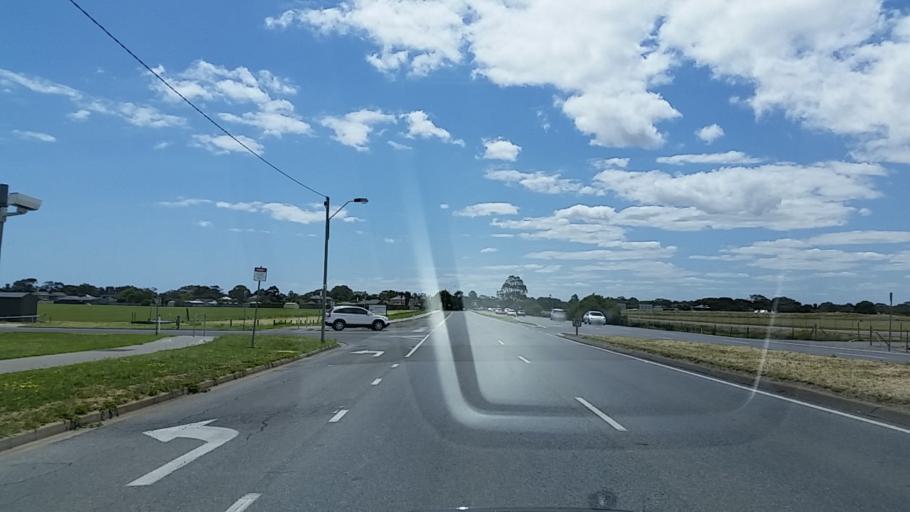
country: AU
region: South Australia
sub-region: Charles Sturt
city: Henley Beach
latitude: -34.9398
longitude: 138.5173
